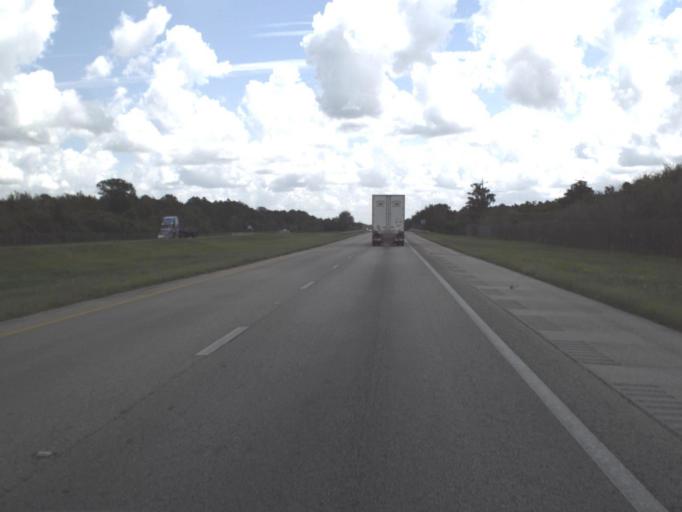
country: US
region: Florida
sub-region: Collier County
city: Orangetree
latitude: 26.1530
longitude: -81.4935
